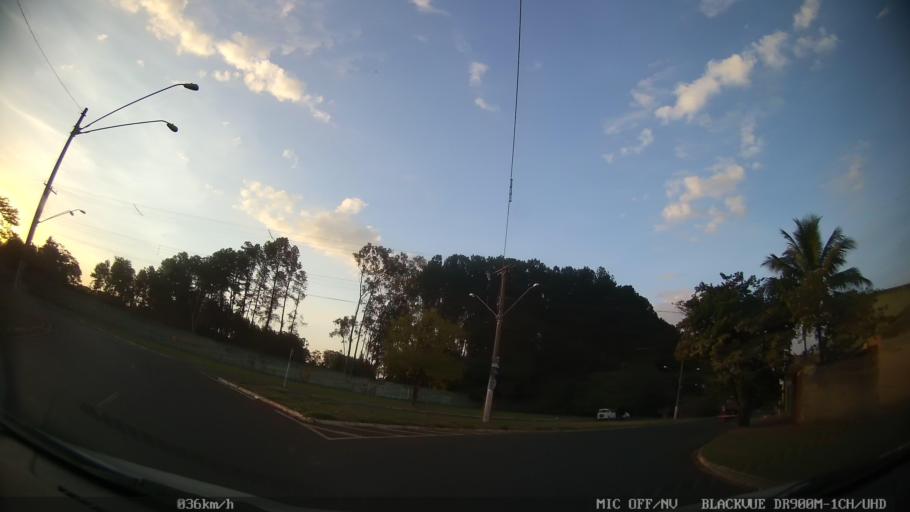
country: BR
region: Sao Paulo
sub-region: Ribeirao Preto
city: Ribeirao Preto
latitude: -21.1299
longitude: -47.8358
